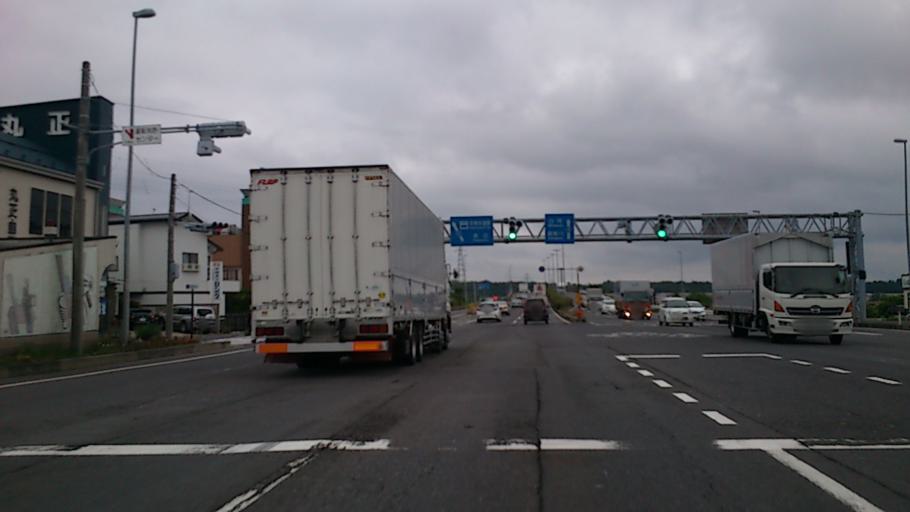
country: JP
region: Fukushima
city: Koriyama
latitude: 37.3727
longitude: 140.3484
